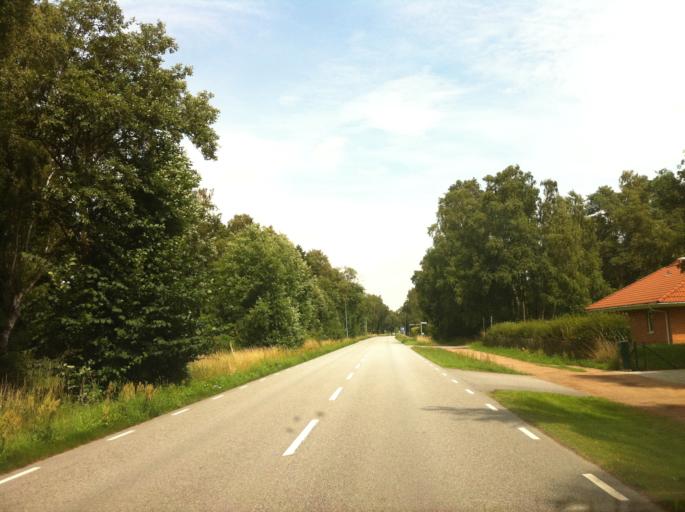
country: SE
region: Skane
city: Smygehamn
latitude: 55.3724
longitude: 13.4520
